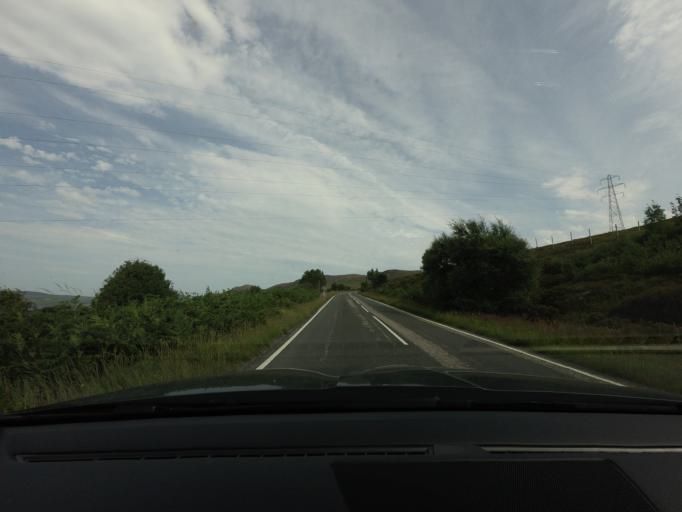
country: GB
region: Scotland
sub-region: Highland
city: Alness
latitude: 57.8431
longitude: -4.2847
